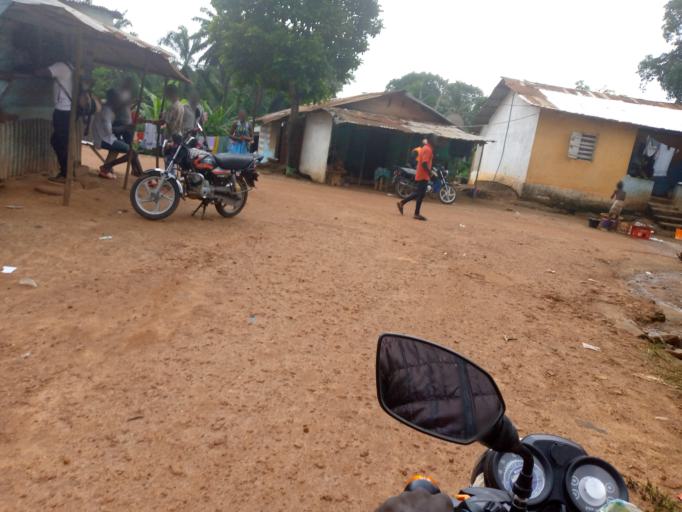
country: SL
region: Eastern Province
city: Kenema
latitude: 7.8760
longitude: -11.1794
